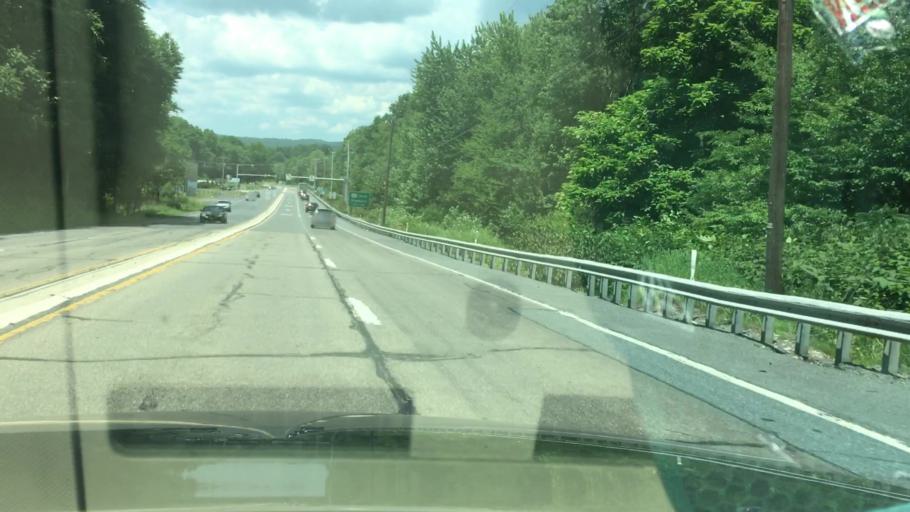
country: US
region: Pennsylvania
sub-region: Schuylkill County
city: Minersville
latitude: 40.6761
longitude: -76.2460
